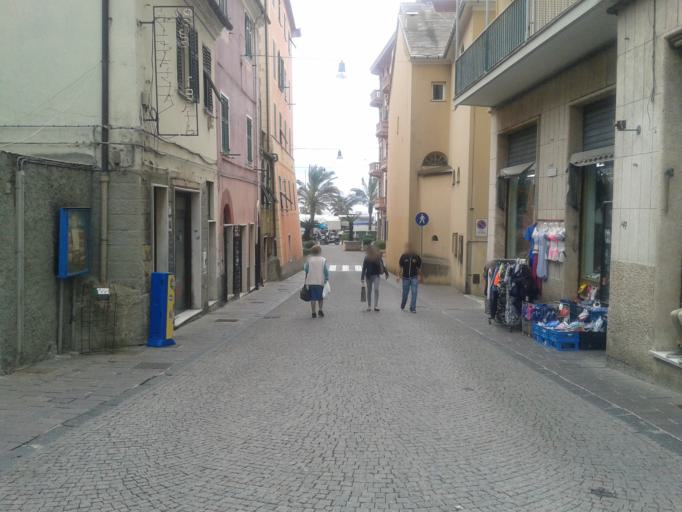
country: IT
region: Liguria
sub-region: Provincia di Genova
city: Cogoleto
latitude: 44.3889
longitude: 8.6441
